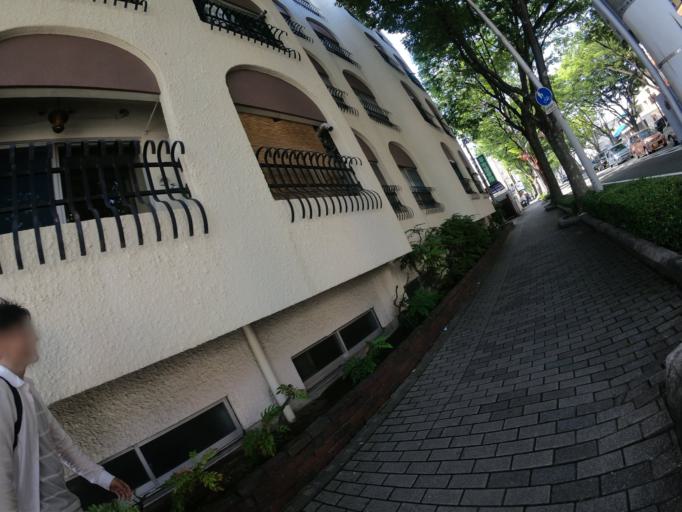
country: JP
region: Osaka
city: Sakai
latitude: 34.5720
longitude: 135.4900
